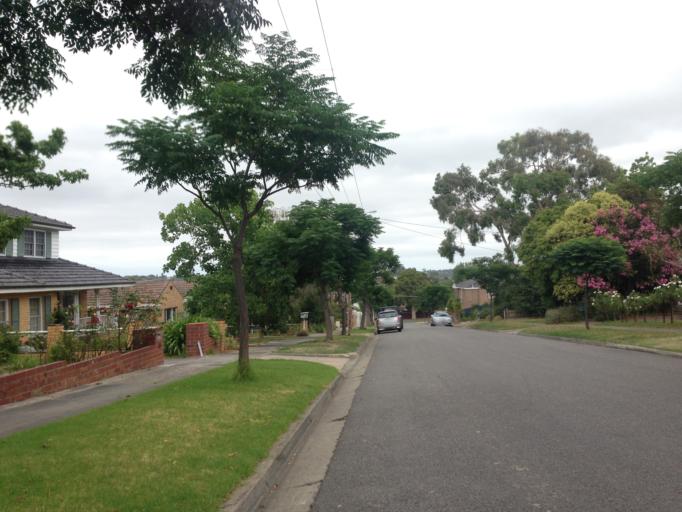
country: AU
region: Victoria
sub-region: Boroondara
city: Balwyn North
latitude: -37.7991
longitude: 145.0915
